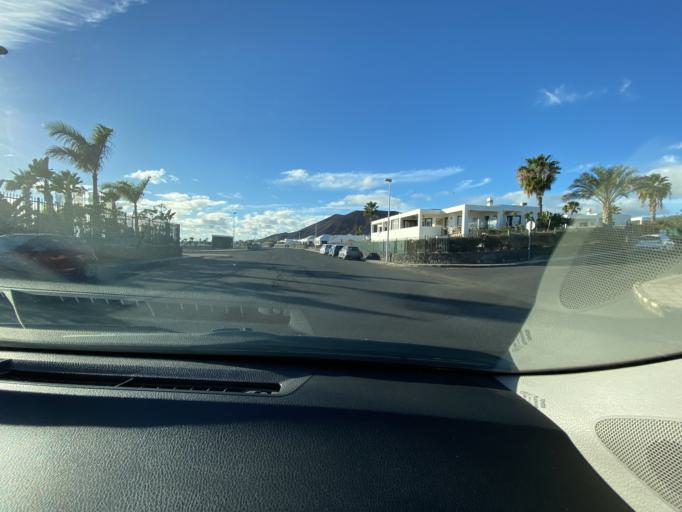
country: ES
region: Canary Islands
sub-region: Provincia de Las Palmas
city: Playa Blanca
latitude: 28.8635
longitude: -13.8434
